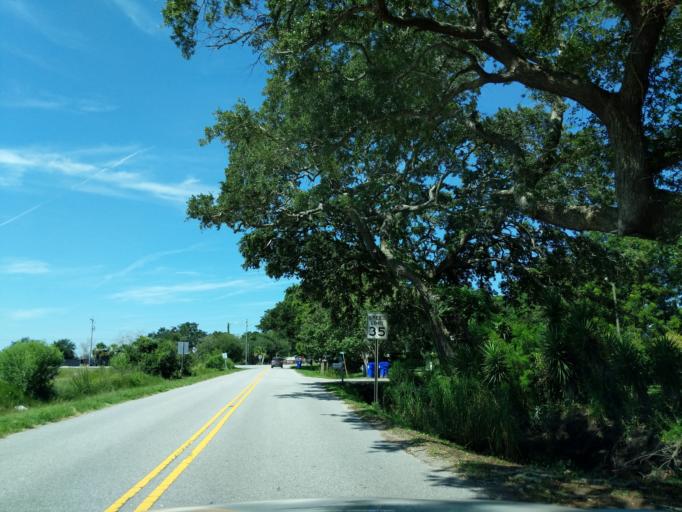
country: US
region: South Carolina
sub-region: Charleston County
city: Folly Beach
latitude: 32.6923
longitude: -79.9628
